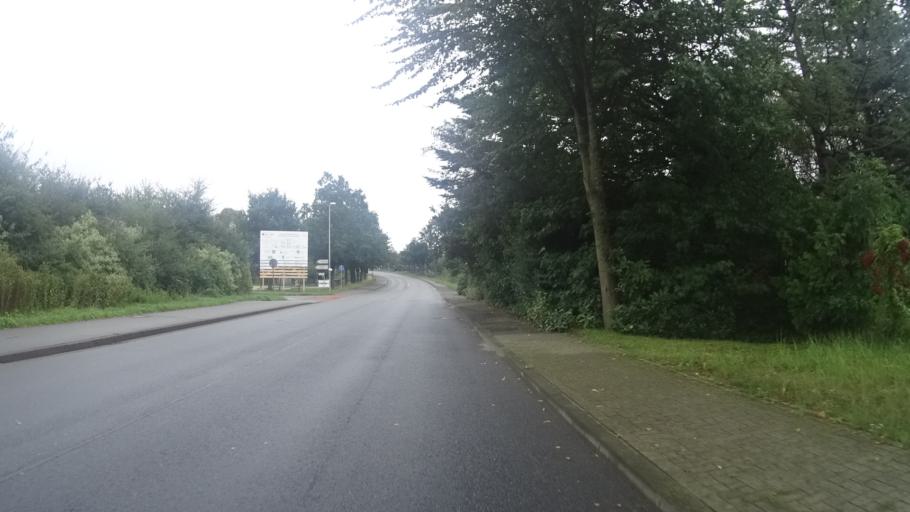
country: DE
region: Schleswig-Holstein
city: Kolln-Reisiek
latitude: 53.7565
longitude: 9.7039
